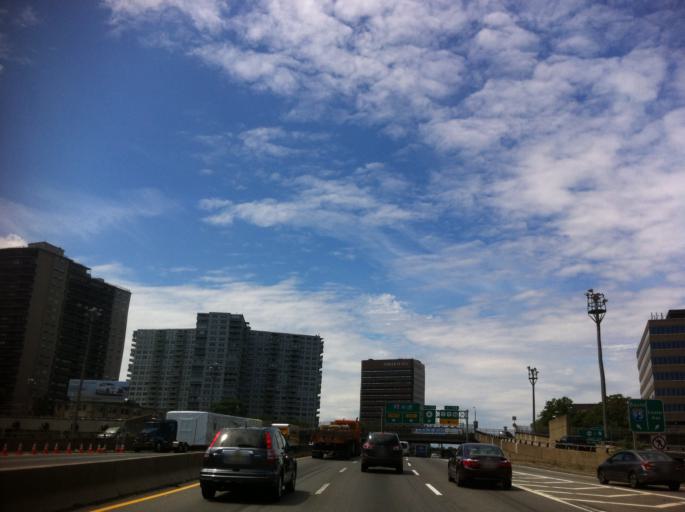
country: US
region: New Jersey
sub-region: Bergen County
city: Fort Lee
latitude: 40.8546
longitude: -73.9668
